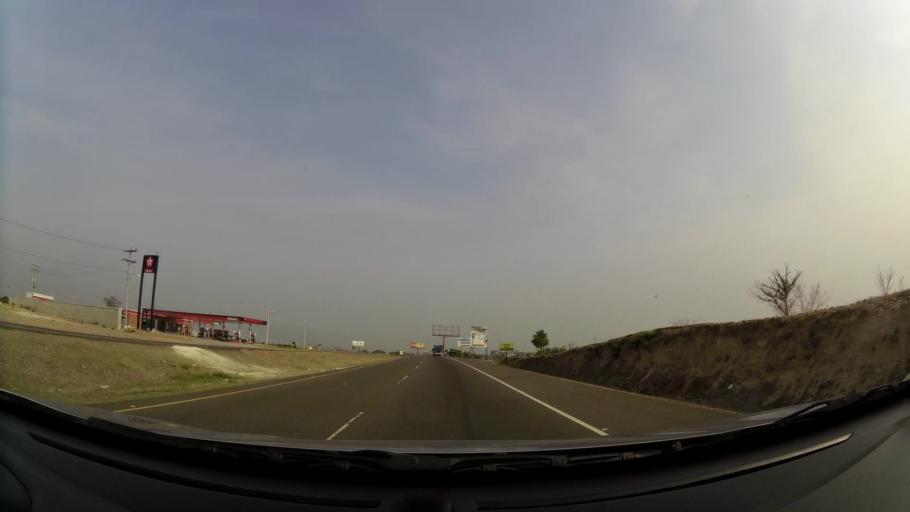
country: HN
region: Comayagua
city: Comayagua
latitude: 14.4217
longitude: -87.6286
